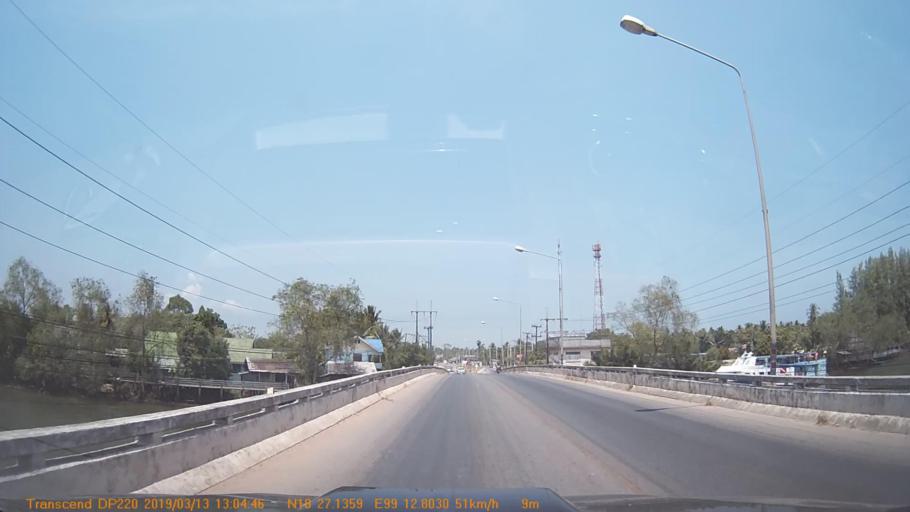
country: TH
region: Chumphon
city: Chumphon
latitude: 10.4526
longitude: 99.2135
